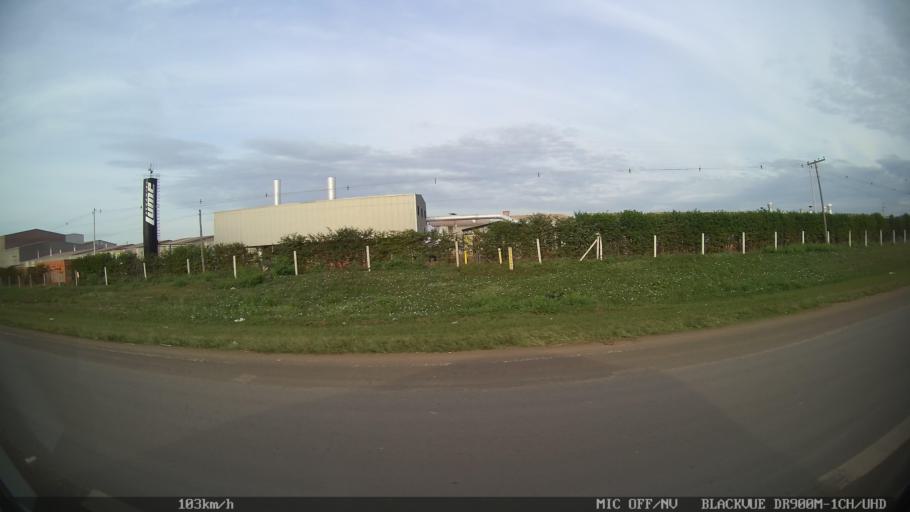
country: BR
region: Sao Paulo
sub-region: Iracemapolis
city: Iracemapolis
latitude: -22.6134
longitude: -47.4790
